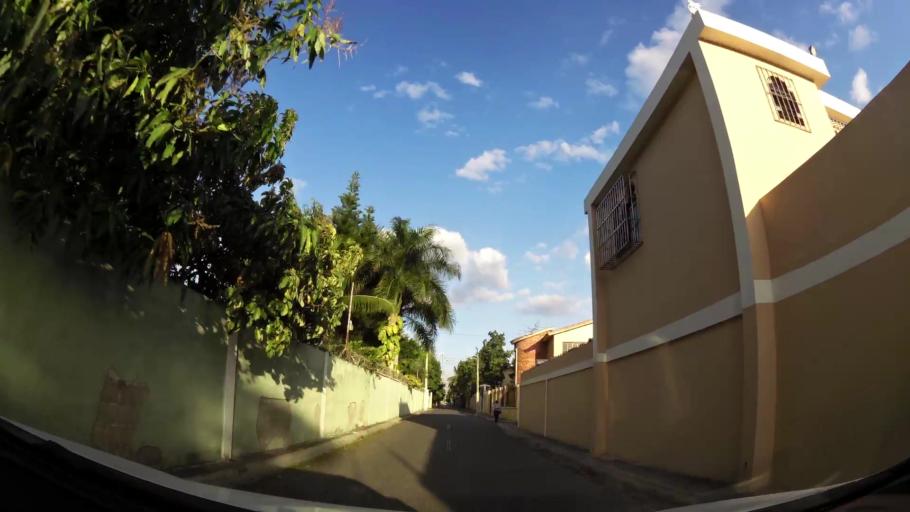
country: DO
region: Santo Domingo
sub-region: Santo Domingo
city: Santo Domingo Este
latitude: 18.4834
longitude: -69.8421
